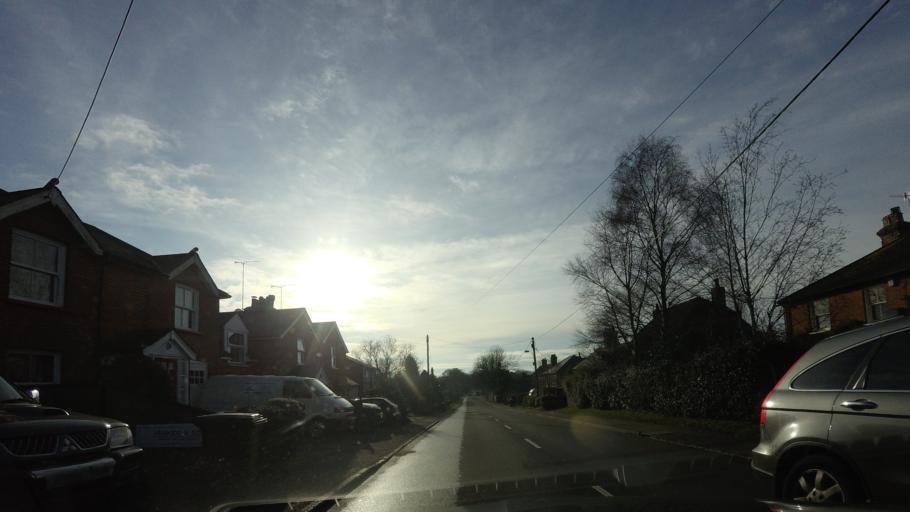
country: GB
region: England
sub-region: East Sussex
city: Battle
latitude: 50.8981
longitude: 0.4499
